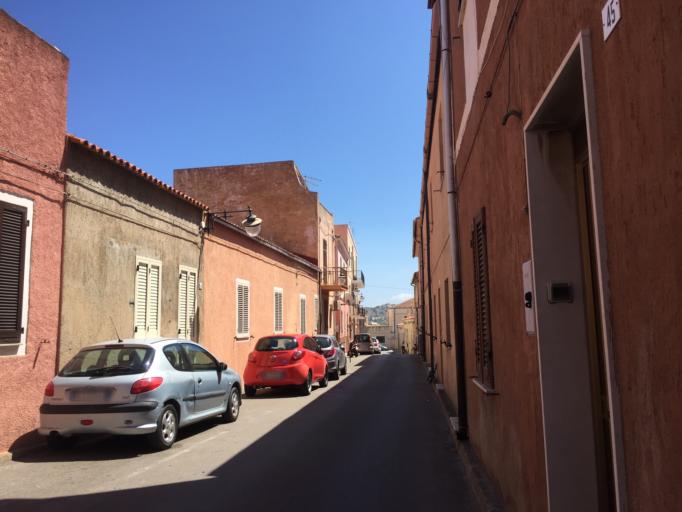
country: IT
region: Sardinia
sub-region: Provincia di Olbia-Tempio
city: La Maddalena
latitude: 41.2163
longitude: 9.4068
